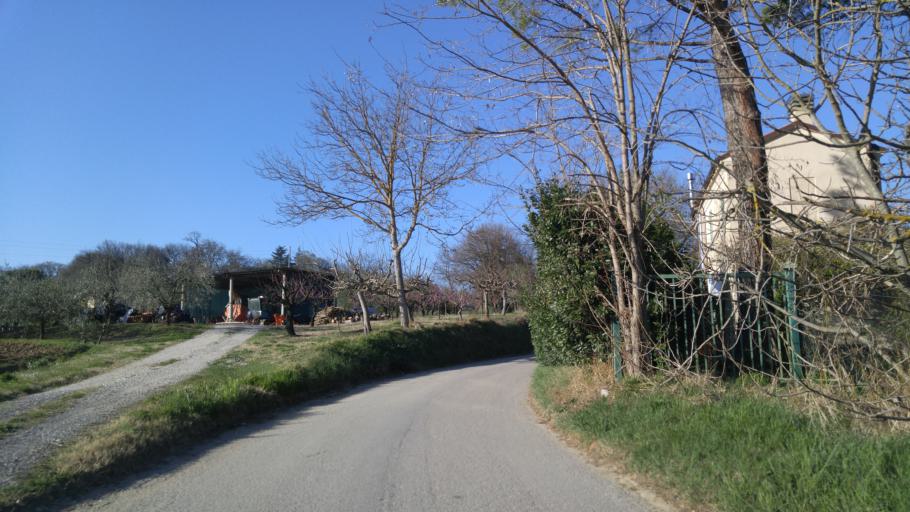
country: IT
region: The Marches
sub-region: Provincia di Pesaro e Urbino
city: Fenile
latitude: 43.8375
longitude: 12.9141
